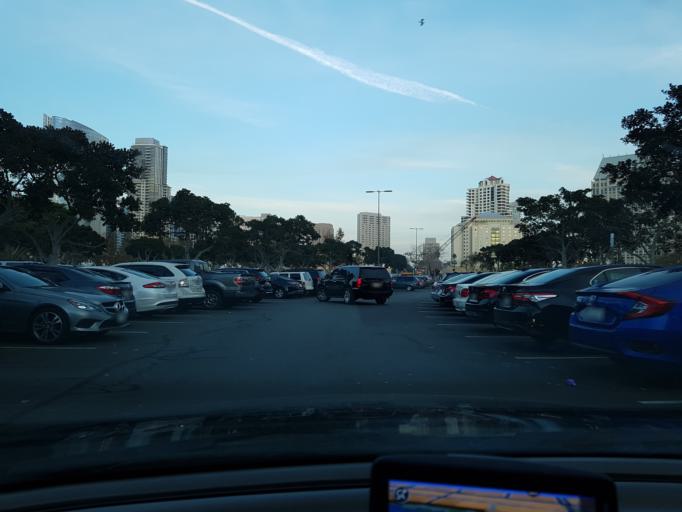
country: US
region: California
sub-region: San Diego County
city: San Diego
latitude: 32.7124
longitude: -117.1753
